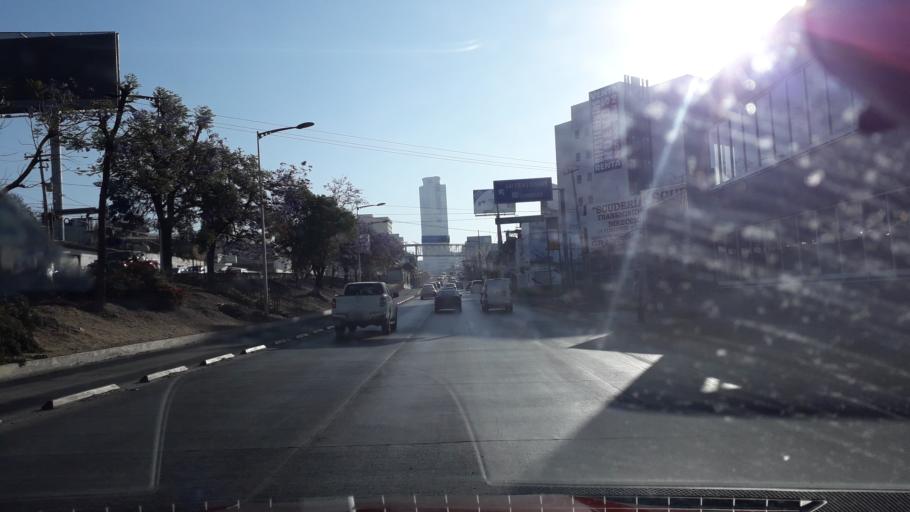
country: MX
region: Puebla
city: Puebla
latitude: 19.0503
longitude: -98.2288
